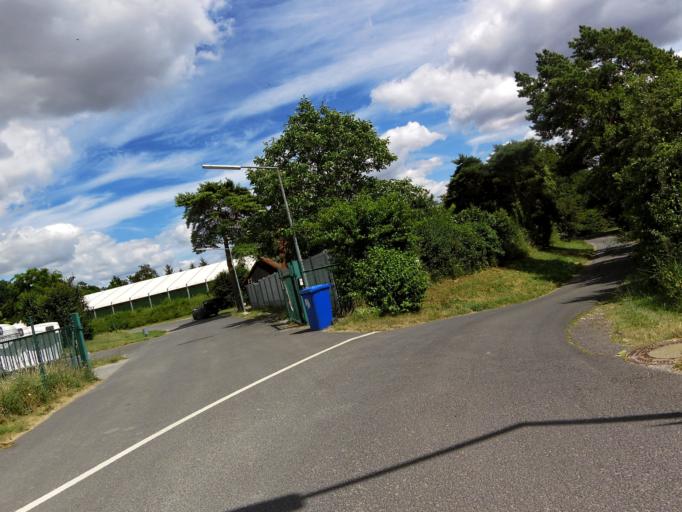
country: DE
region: Bavaria
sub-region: Regierungsbezirk Unterfranken
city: Gadheim
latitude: 49.8139
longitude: 9.9092
